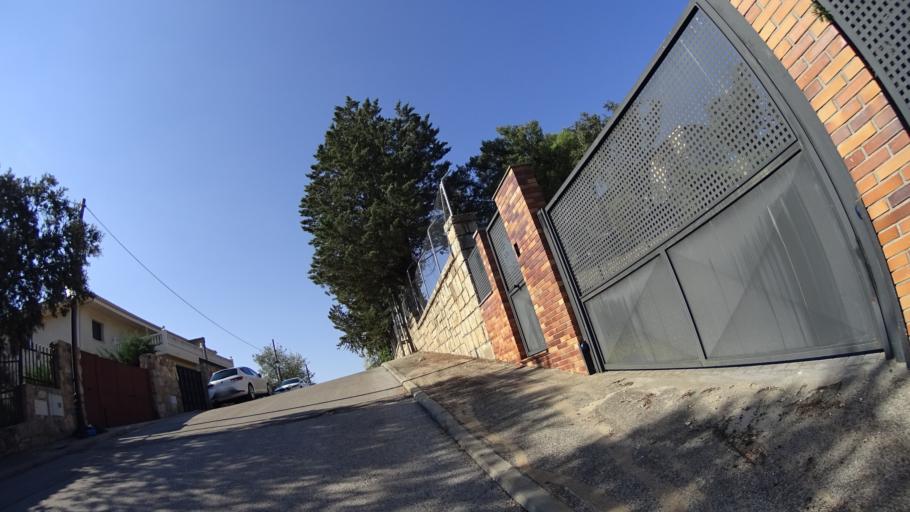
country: ES
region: Madrid
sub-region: Provincia de Madrid
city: Torrelodones
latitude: 40.5754
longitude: -3.9077
